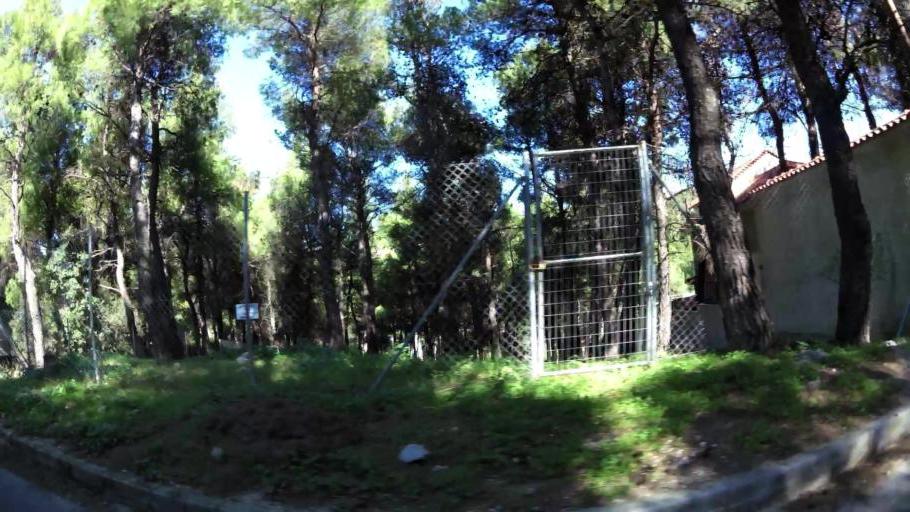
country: GR
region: Attica
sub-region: Nomarchia Anatolikis Attikis
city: Dionysos
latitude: 38.1047
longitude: 23.8866
